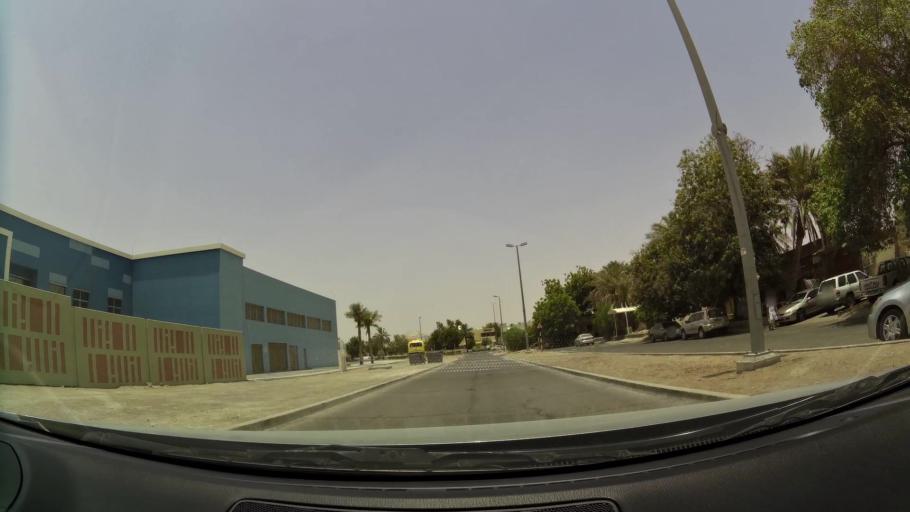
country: AE
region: Abu Dhabi
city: Al Ain
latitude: 24.2100
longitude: 55.7479
